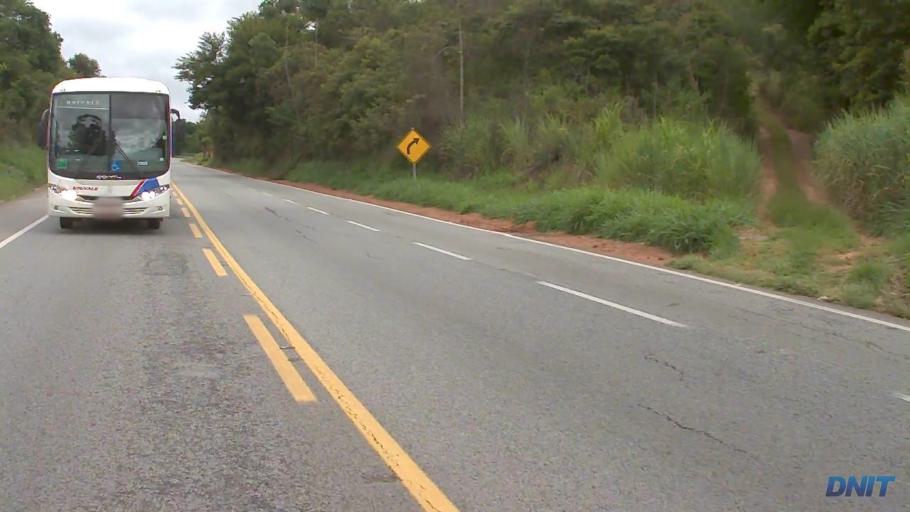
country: BR
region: Minas Gerais
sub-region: Joao Monlevade
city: Joao Monlevade
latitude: -19.8441
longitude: -43.3084
